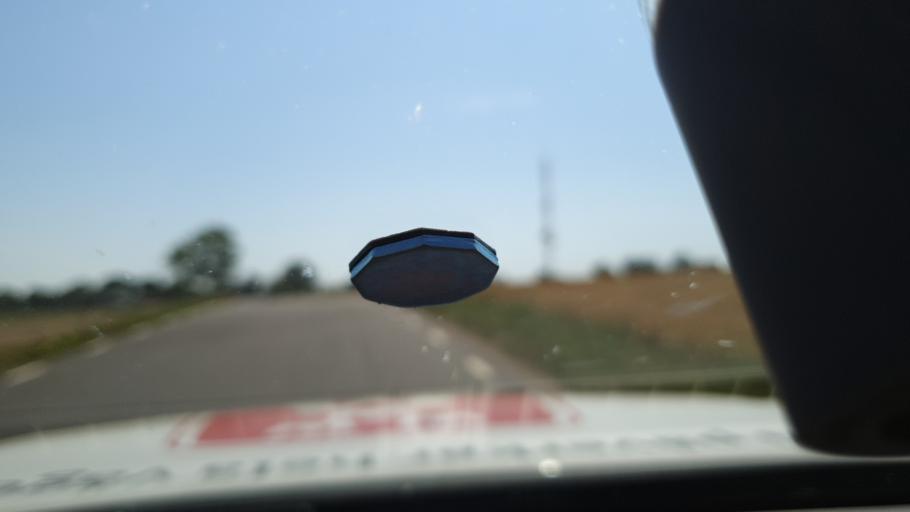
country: SE
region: Skane
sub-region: Sjobo Kommun
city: Blentarp
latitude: 55.5488
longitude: 13.5590
